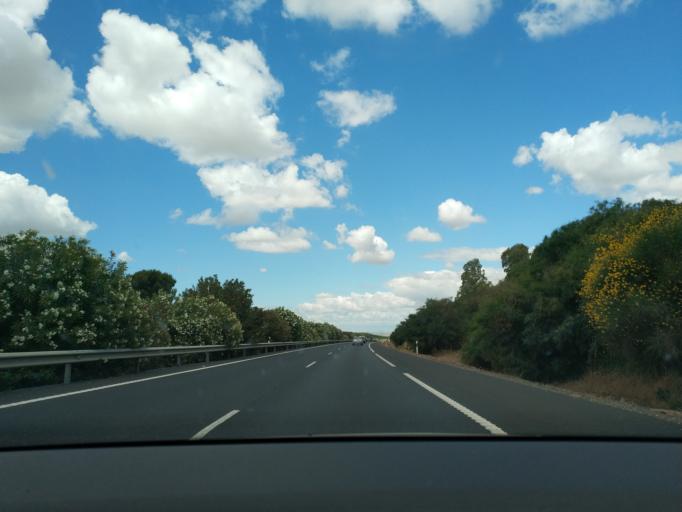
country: ES
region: Andalusia
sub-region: Provincia de Huelva
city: Niebla
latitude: 37.3437
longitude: -6.6368
